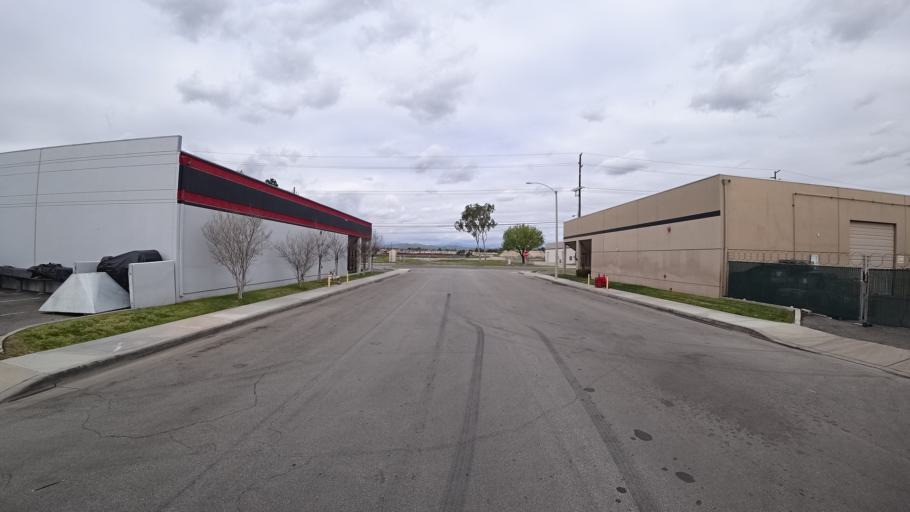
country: US
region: California
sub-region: Orange County
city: Placentia
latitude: 33.8615
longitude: -117.8434
